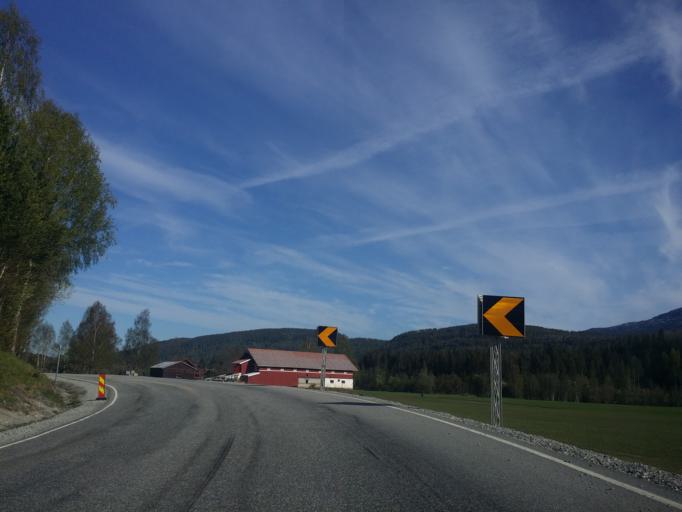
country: NO
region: Telemark
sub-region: Hjartdal
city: Sauland
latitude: 59.6214
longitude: 8.9119
